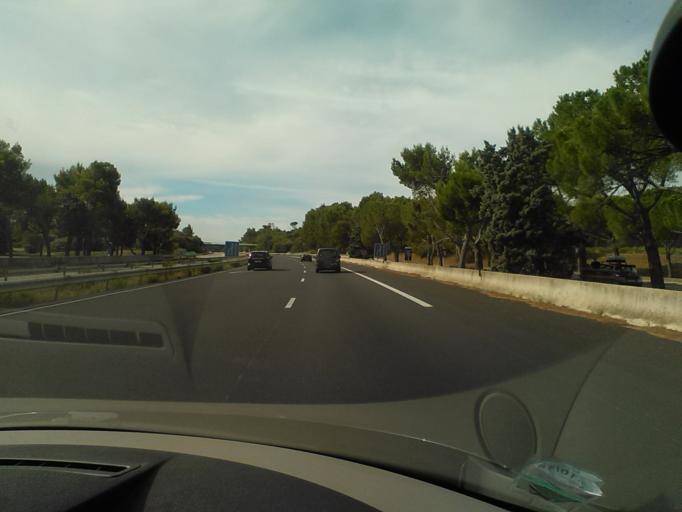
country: FR
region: Languedoc-Roussillon
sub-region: Departement du Gard
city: Roquemaure
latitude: 44.0493
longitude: 4.7647
